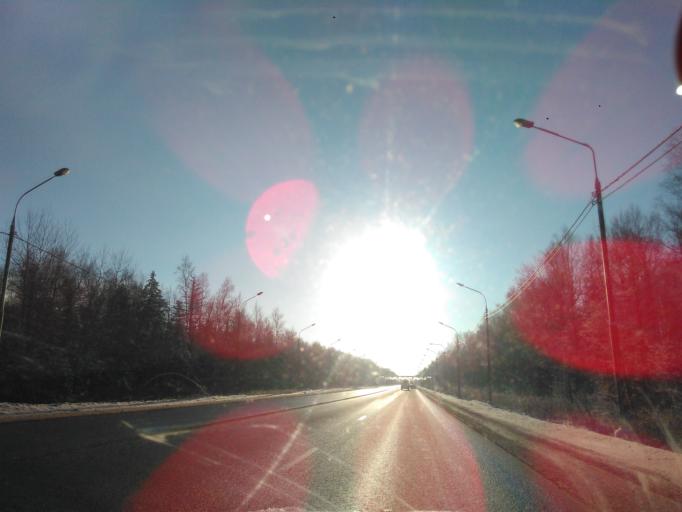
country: RU
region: Moskovskaya
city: Reshetnikovo
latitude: 56.4142
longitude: 36.6390
